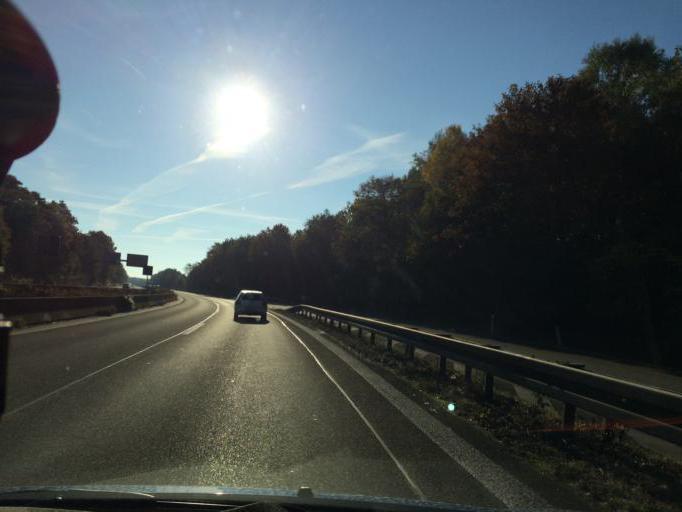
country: DE
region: North Rhine-Westphalia
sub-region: Regierungsbezirk Koln
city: Ostheim
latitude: 50.9142
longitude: 7.0293
